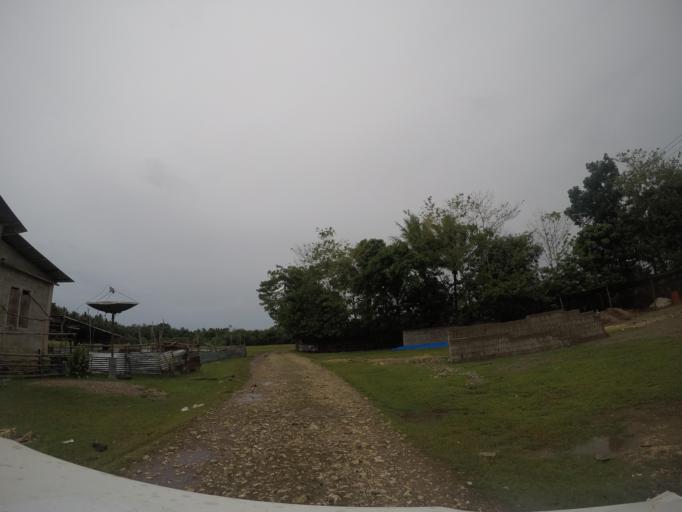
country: TL
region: Lautem
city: Lospalos
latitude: -8.5267
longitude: 127.0033
